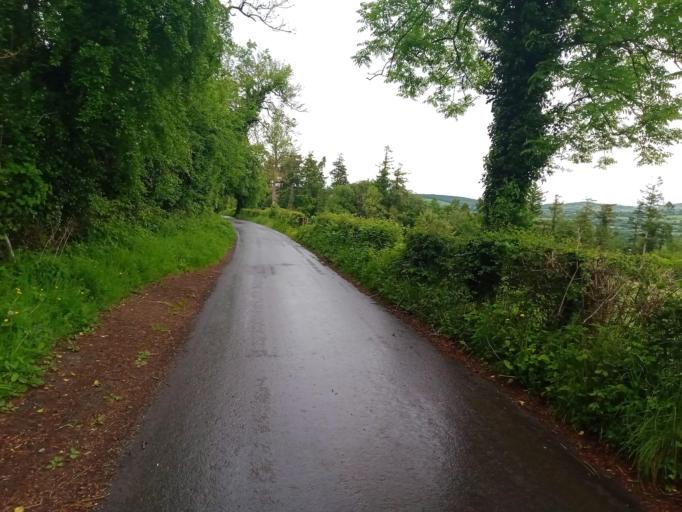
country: IE
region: Leinster
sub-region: Kilkenny
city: Thomastown
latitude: 52.4798
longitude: -7.0639
